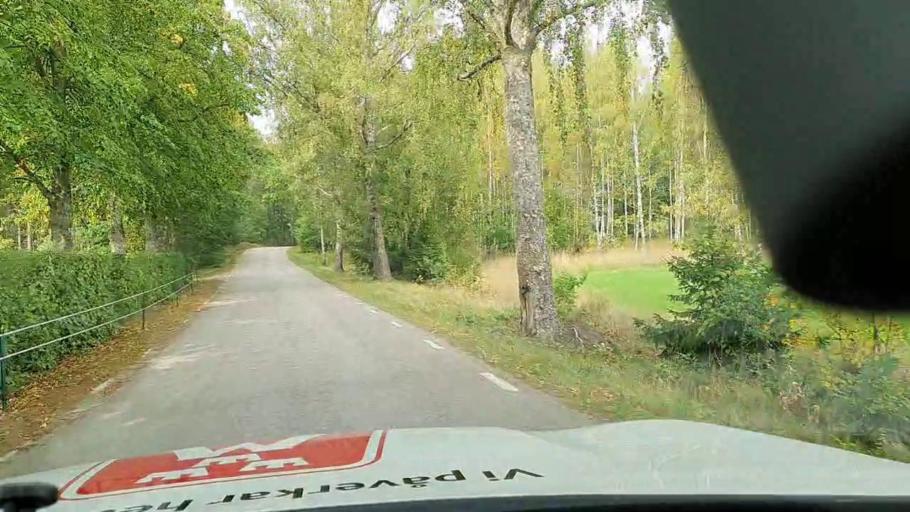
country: SE
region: Soedermanland
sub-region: Nykopings Kommun
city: Svalsta
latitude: 58.8299
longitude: 16.8827
